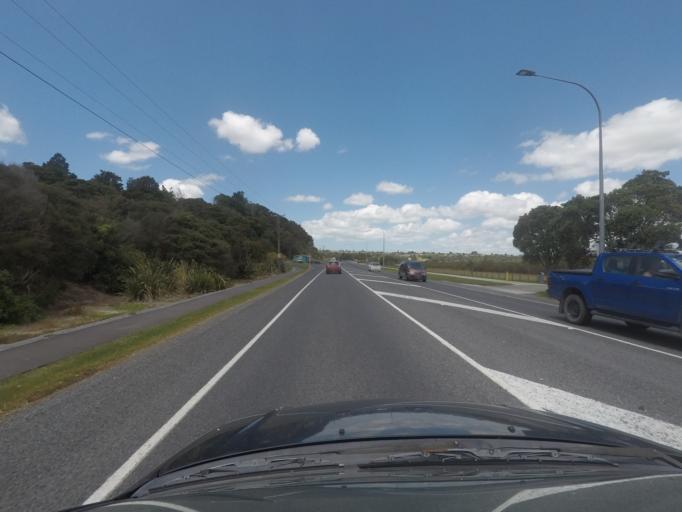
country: NZ
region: Northland
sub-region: Whangarei
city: Whangarei
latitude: -35.7349
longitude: 174.3504
